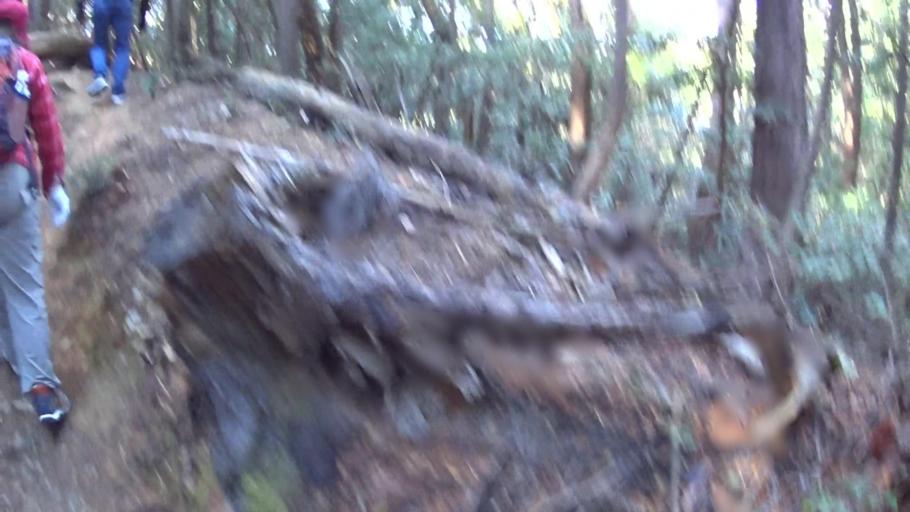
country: JP
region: Kyoto
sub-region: Kyoto-shi
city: Kamigyo-ku
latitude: 35.0964
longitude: 135.7577
